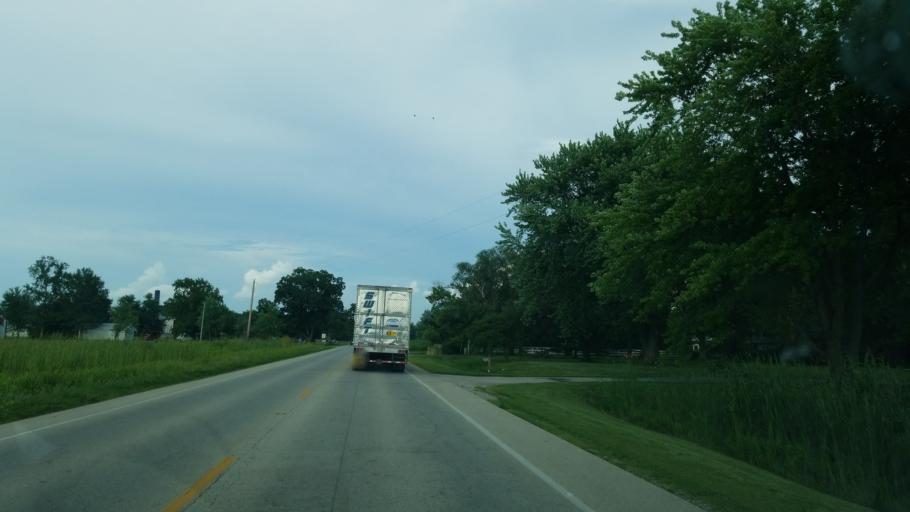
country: US
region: Illinois
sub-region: Marion County
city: Sandoval
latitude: 38.6164
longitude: -89.1346
